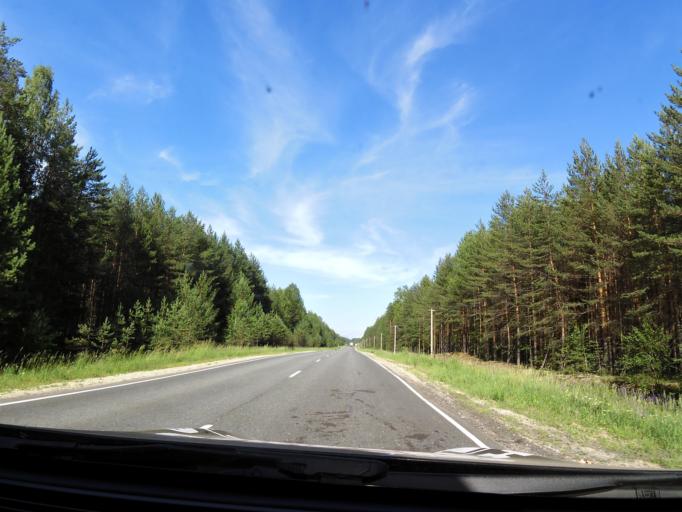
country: RU
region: Kirov
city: Belaya Kholunitsa
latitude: 58.9091
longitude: 51.0541
